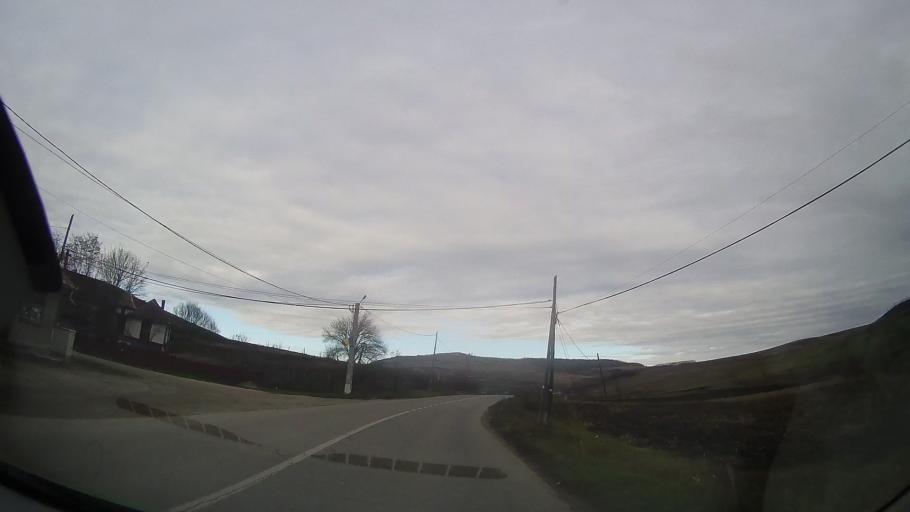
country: RO
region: Cluj
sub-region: Comuna Camarasu
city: Camarasu
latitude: 46.8191
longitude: 24.1365
